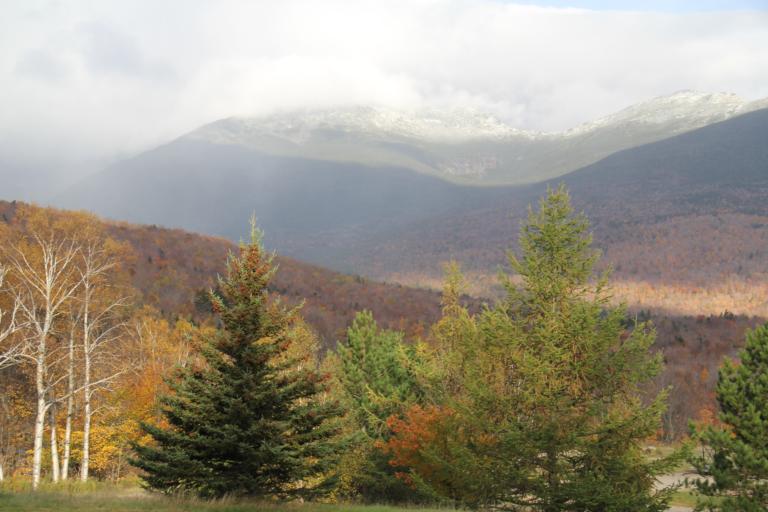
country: US
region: New Hampshire
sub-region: Coos County
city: Gorham
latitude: 44.2897
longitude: -71.2244
